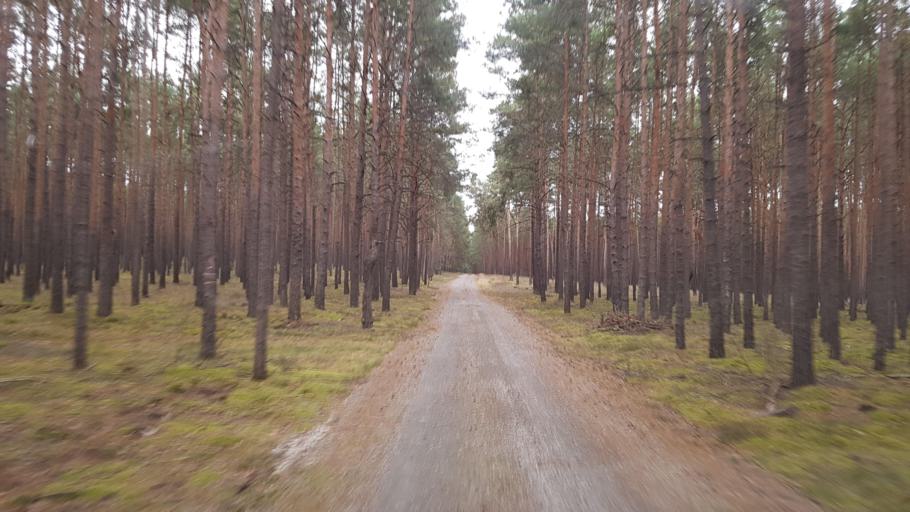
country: DE
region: Brandenburg
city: Sonnewalde
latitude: 51.7440
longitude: 13.6540
